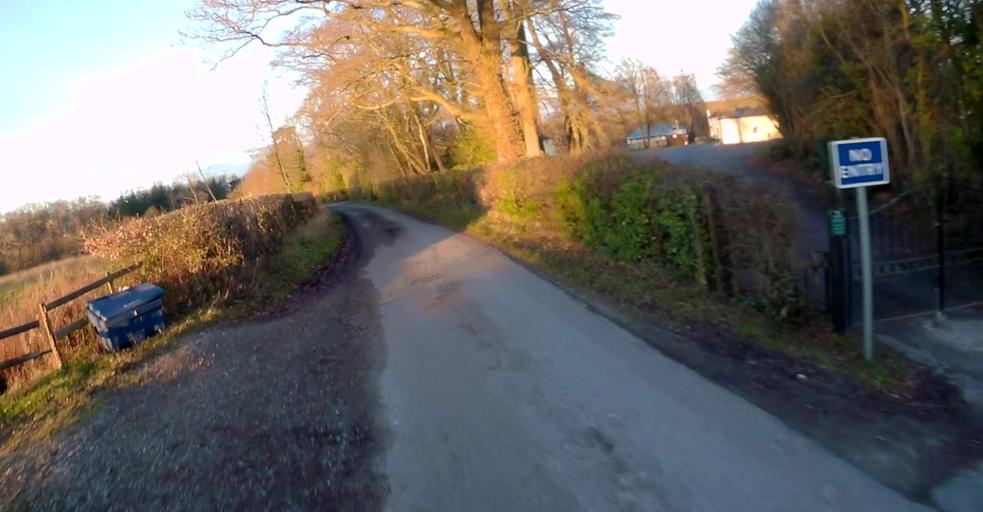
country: GB
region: England
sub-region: Hampshire
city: Hook
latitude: 51.3303
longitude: -0.9884
